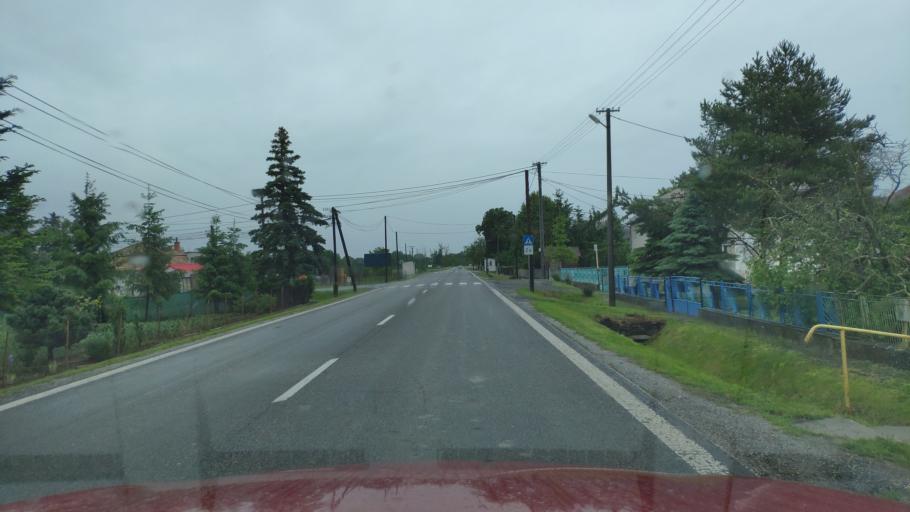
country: HU
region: Borsod-Abauj-Zemplen
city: Karcsa
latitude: 48.4279
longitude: 21.8461
